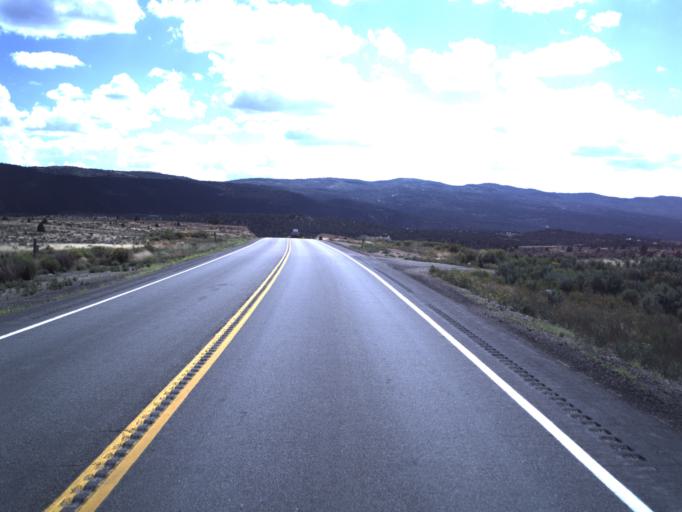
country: US
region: Utah
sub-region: Duchesne County
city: Duchesne
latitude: 40.2046
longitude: -110.7723
